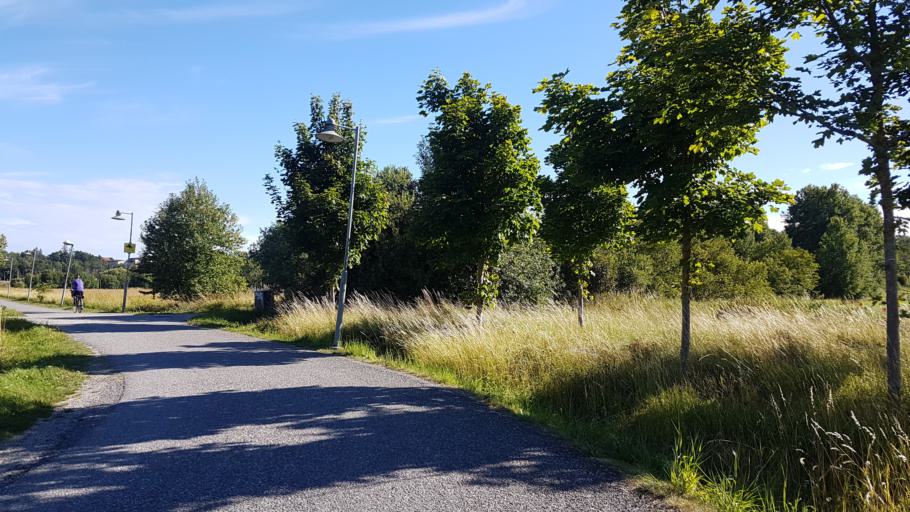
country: SE
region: Stockholm
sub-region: Stockholms Kommun
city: Arsta
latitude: 59.2903
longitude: 18.0419
